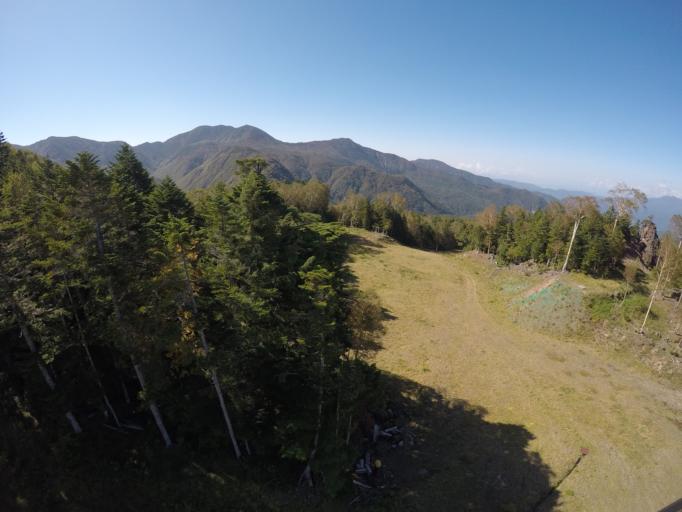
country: JP
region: Tochigi
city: Nikko
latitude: 36.8072
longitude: 139.3536
